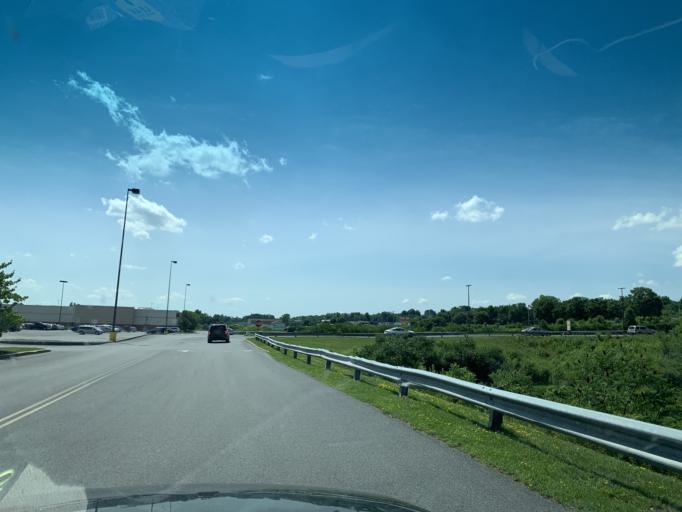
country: US
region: New York
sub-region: Oneida County
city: New Hartford
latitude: 43.0849
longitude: -75.3134
